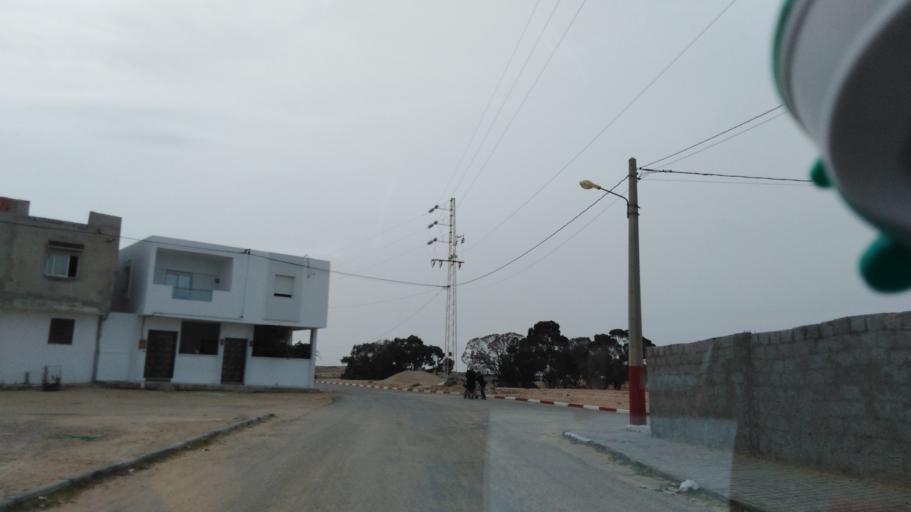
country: TN
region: Qabis
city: Gabes
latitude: 33.9530
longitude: 10.0037
